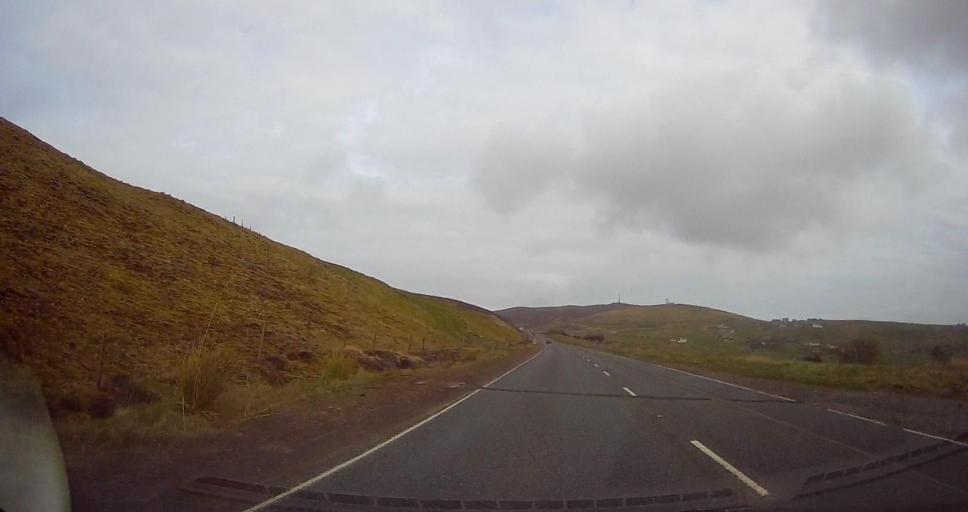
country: GB
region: Scotland
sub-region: Shetland Islands
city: Lerwick
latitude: 60.1282
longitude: -1.2160
